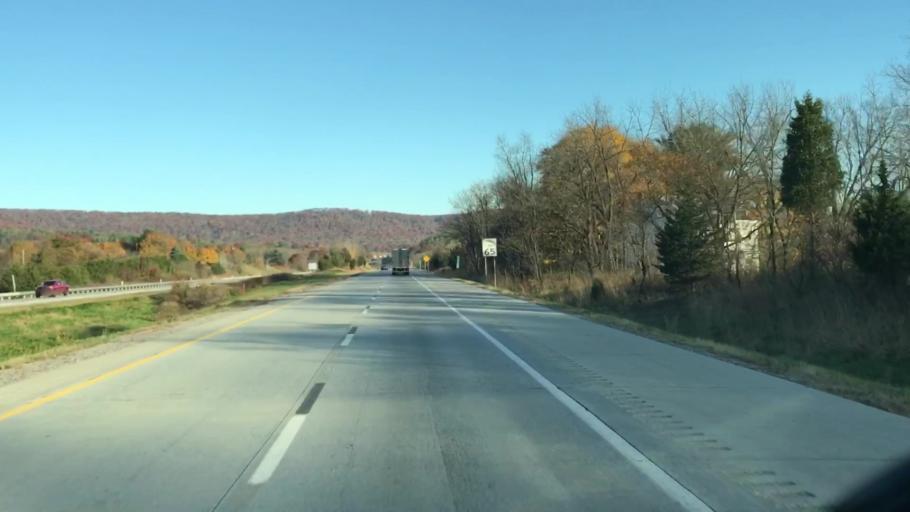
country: US
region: Pennsylvania
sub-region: Schuylkill County
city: Pine Grove
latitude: 40.5431
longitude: -76.4296
